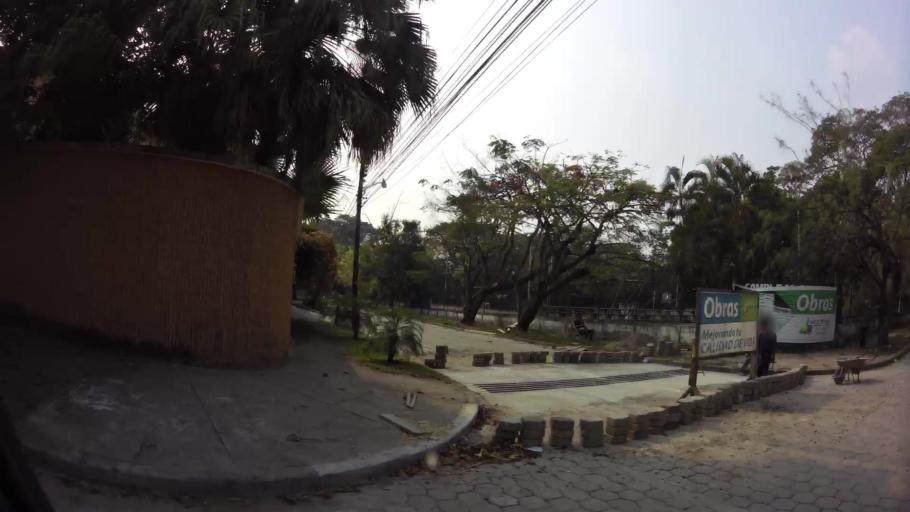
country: HN
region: Cortes
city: El Zapotal del Norte
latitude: 15.5187
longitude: -88.0453
